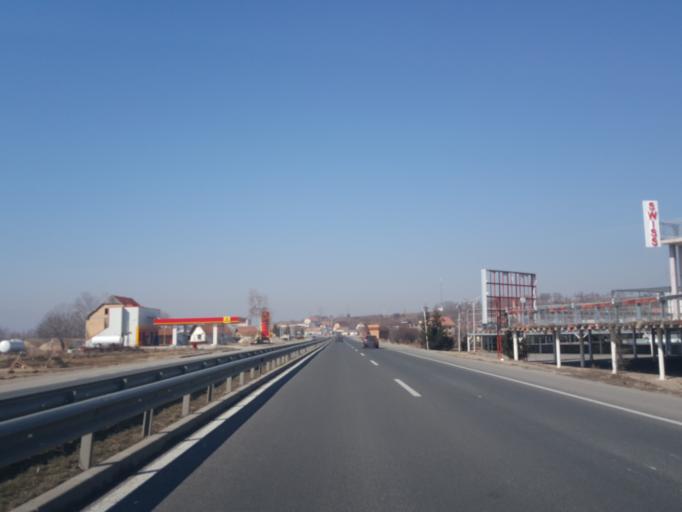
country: XK
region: Pristina
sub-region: Komuna e Obiliqit
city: Obiliq
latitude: 42.7359
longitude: 21.0647
